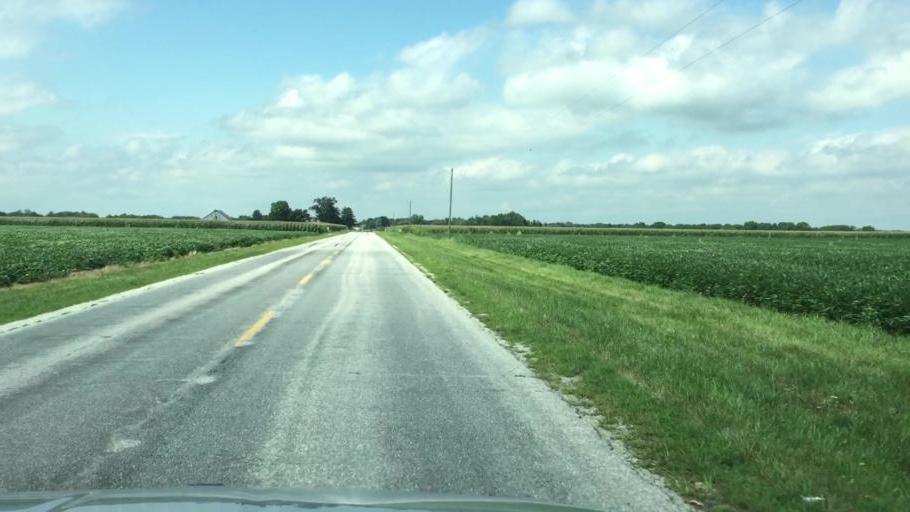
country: US
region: Illinois
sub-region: Hancock County
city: Nauvoo
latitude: 40.5127
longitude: -91.3082
